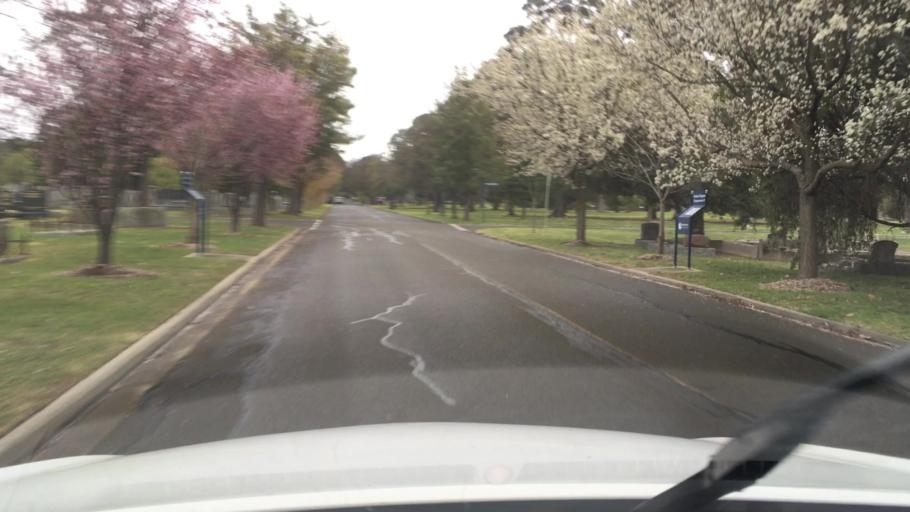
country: AU
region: Victoria
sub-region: Greater Dandenong
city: Noble Park North
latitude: -37.9441
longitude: 145.1818
